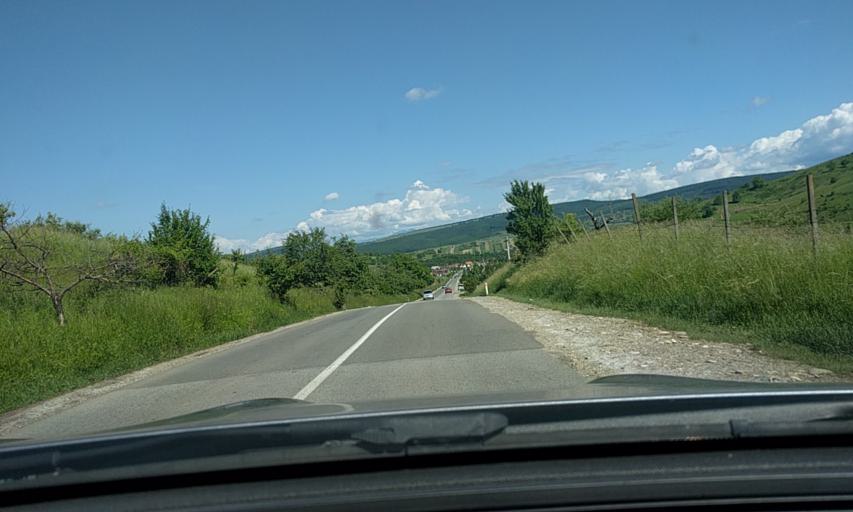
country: RO
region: Bistrita-Nasaud
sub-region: Comuna Dumitra
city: Dumitra
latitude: 47.2077
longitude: 24.4722
